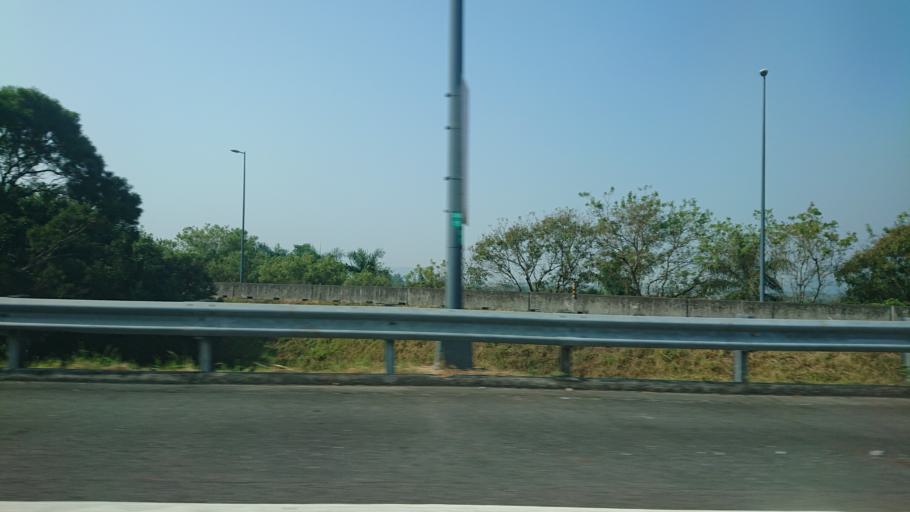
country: TW
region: Taiwan
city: Lugu
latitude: 23.7984
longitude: 120.7006
